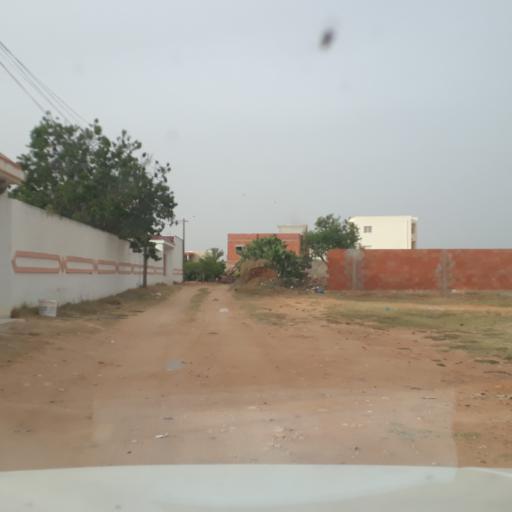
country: TN
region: Safaqis
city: Al Qarmadah
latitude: 34.8195
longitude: 10.7700
